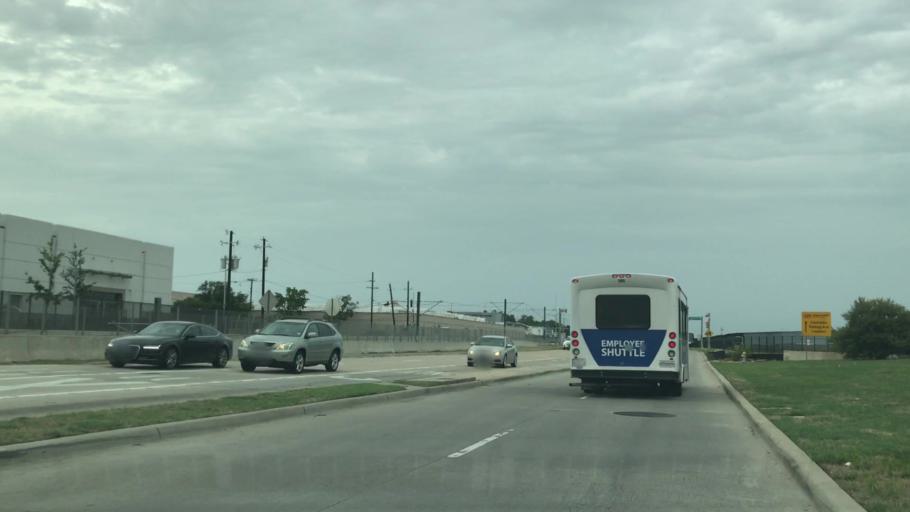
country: US
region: Texas
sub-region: Dallas County
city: University Park
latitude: 32.8305
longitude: -96.8419
